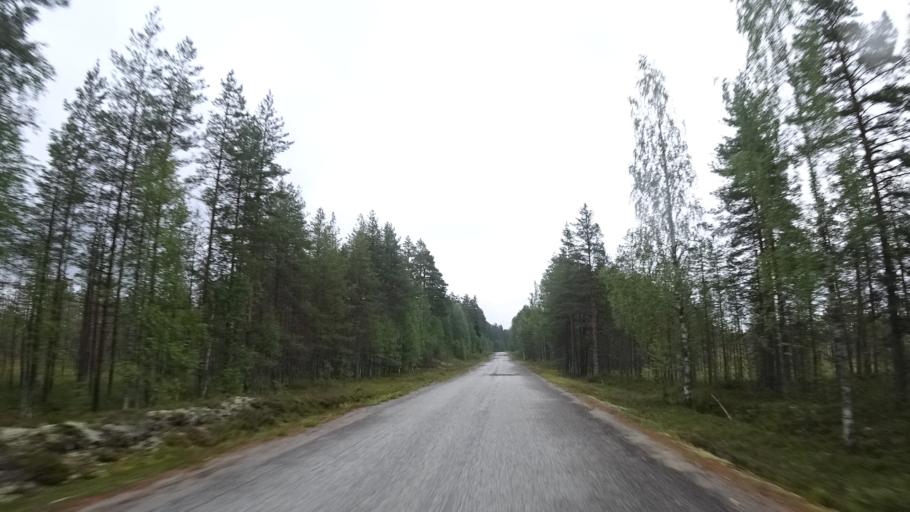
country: FI
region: North Karelia
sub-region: Joensuu
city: Ilomantsi
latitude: 63.2277
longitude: 30.8659
